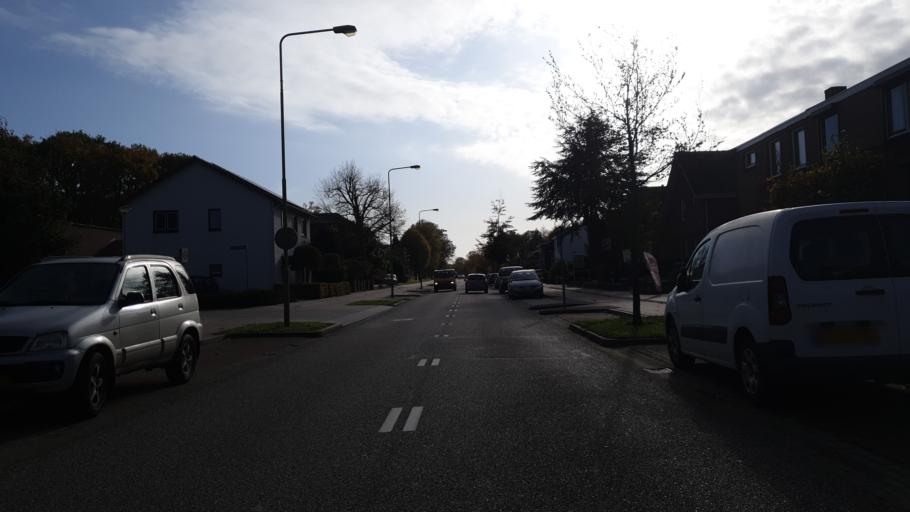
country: NL
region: Limburg
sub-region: Gemeente Gennep
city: Gennep
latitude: 51.6927
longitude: 5.9730
